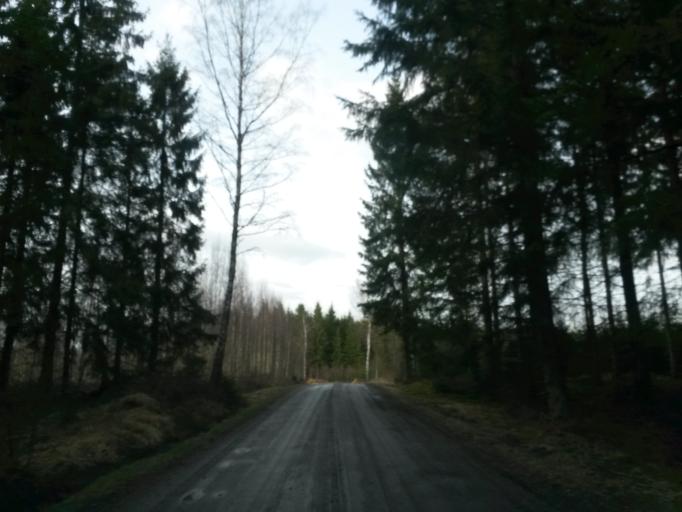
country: SE
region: Vaestra Goetaland
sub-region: Vargarda Kommun
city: Vargarda
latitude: 58.0068
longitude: 12.7716
